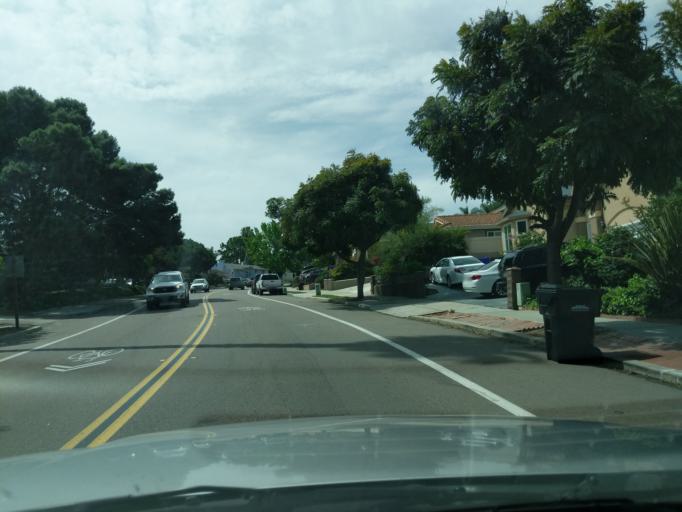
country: US
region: California
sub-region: San Diego County
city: Coronado
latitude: 32.7419
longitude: -117.2362
